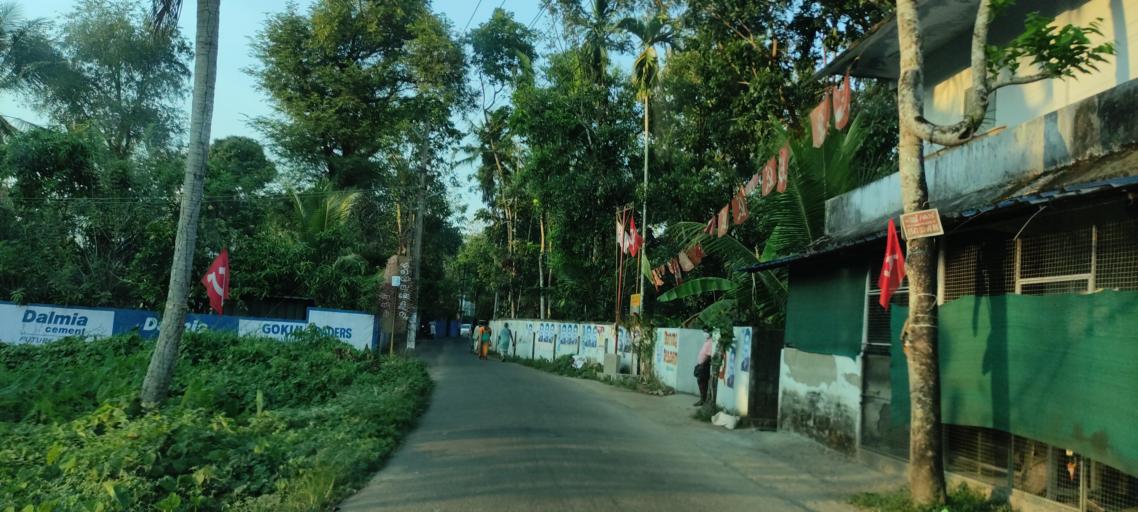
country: IN
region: Kerala
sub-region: Alappuzha
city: Kutiatodu
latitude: 9.7849
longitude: 76.3241
